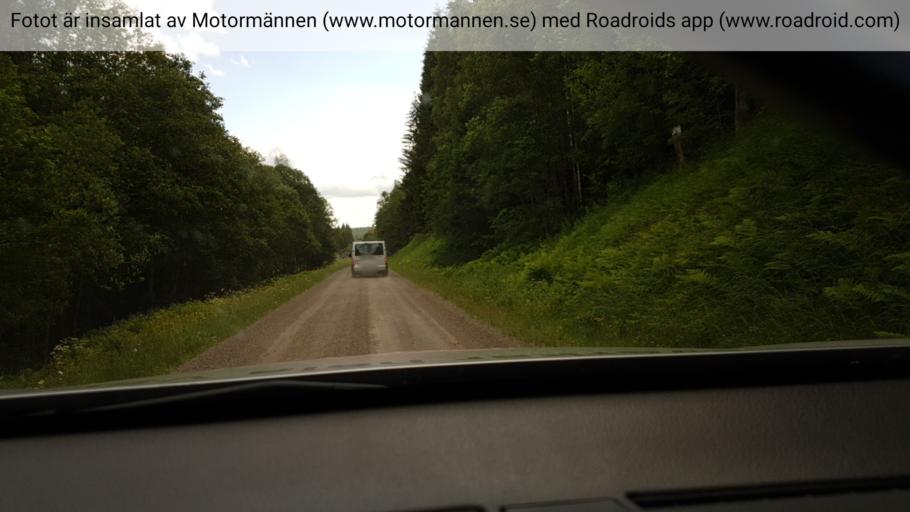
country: SE
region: Vaermland
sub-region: Hagfors Kommun
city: Ekshaerad
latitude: 60.3356
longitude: 13.3470
